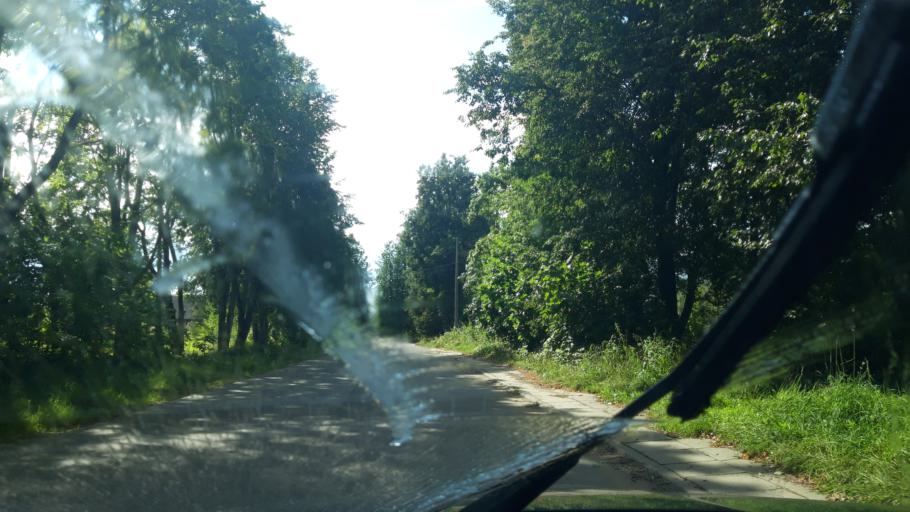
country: RU
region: Moskovskaya
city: Chashnikovo
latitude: 56.0350
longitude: 37.1700
